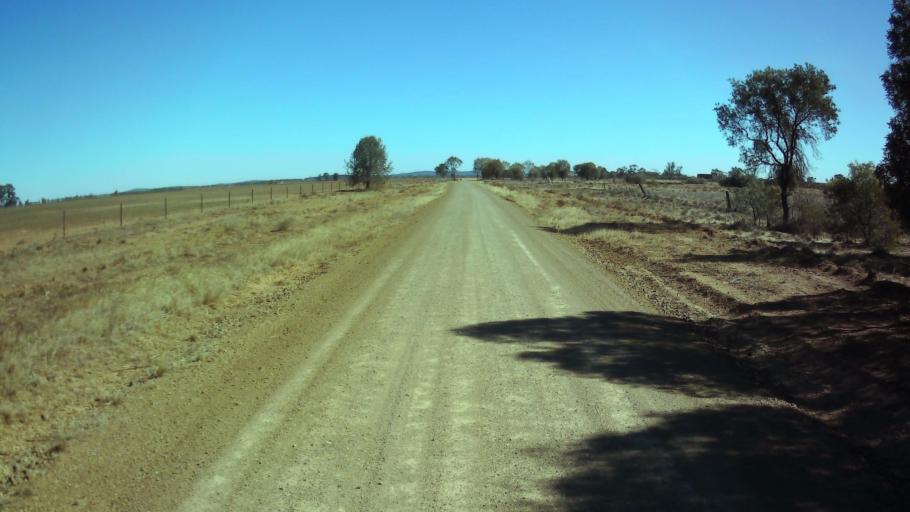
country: AU
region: New South Wales
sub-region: Weddin
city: Grenfell
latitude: -33.8385
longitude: 147.7415
